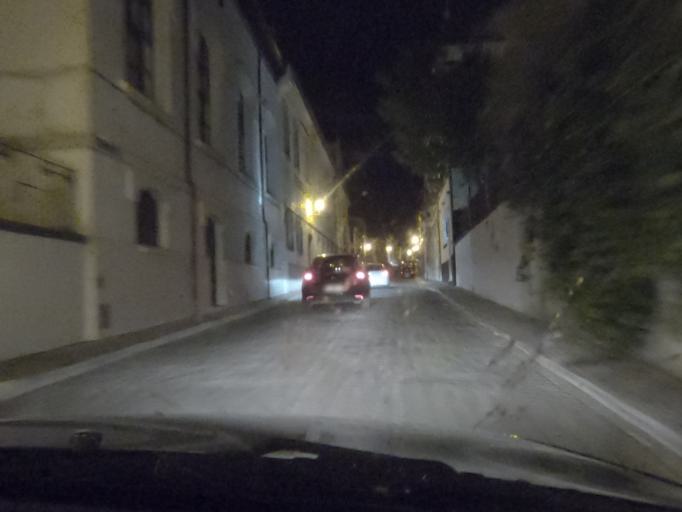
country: PT
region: Evora
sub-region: Estremoz
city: Estremoz
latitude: 38.8455
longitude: -7.5911
